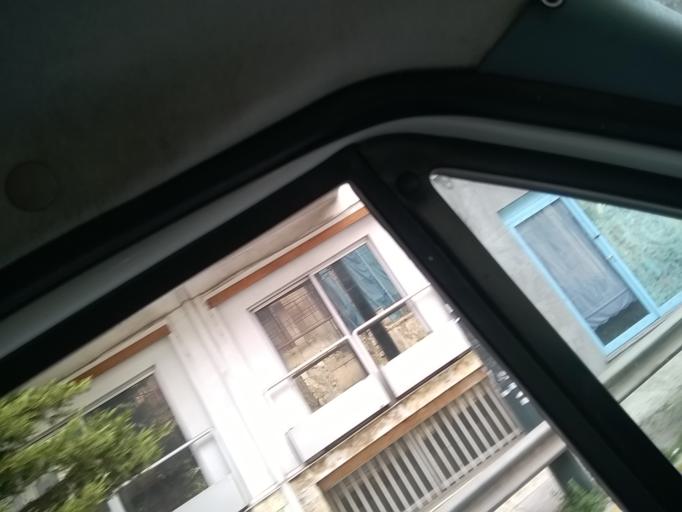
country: GR
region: Attica
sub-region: Nomos Attikis
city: Piraeus
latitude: 37.9371
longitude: 23.6575
